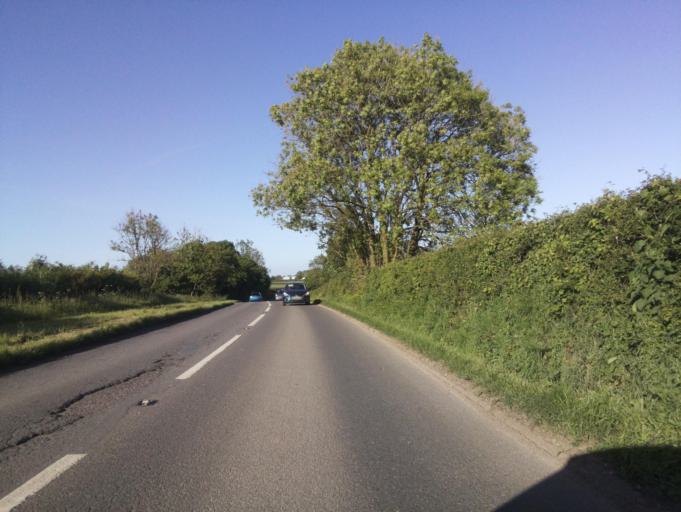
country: GB
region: England
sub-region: Devon
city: Sidmouth
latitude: 50.7152
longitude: -3.1631
